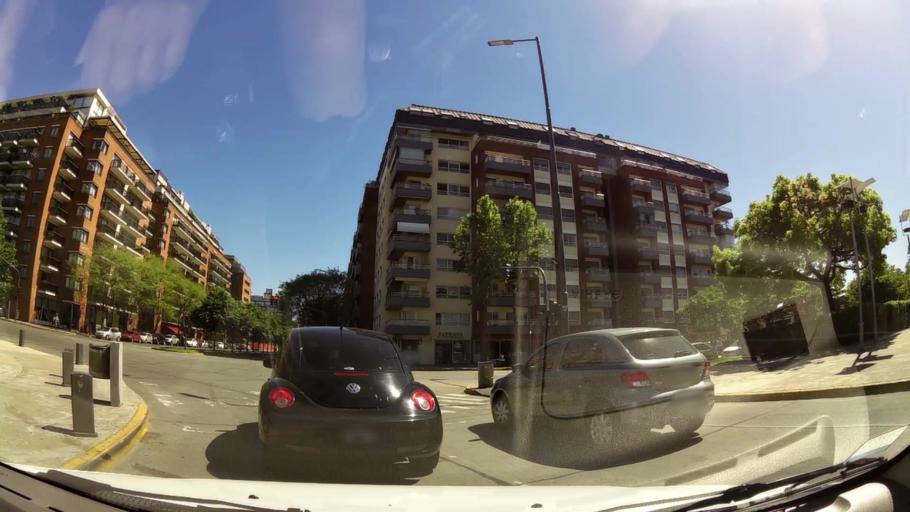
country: AR
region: Buenos Aires F.D.
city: Buenos Aires
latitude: -34.6177
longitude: -58.3617
